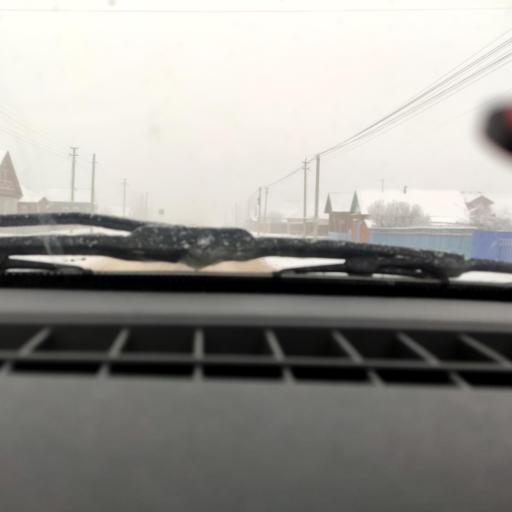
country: RU
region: Bashkortostan
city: Kabakovo
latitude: 54.6923
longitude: 56.1354
